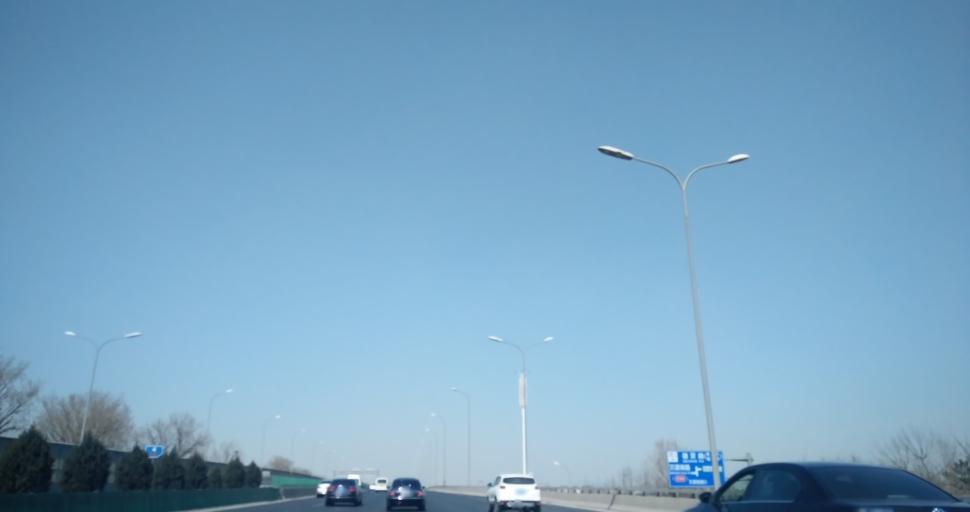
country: CN
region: Beijing
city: Jiugong
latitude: 39.7956
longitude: 116.4238
